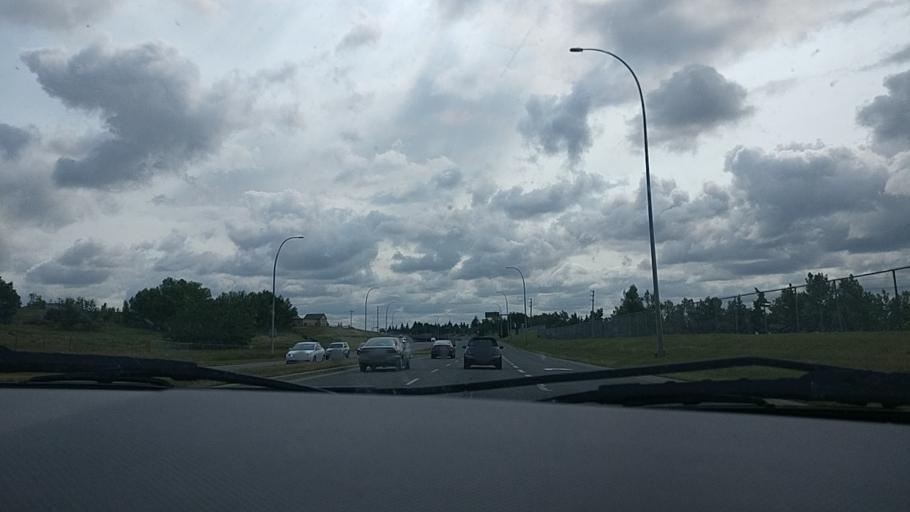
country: CA
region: Alberta
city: Calgary
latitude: 51.0916
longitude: -114.1019
